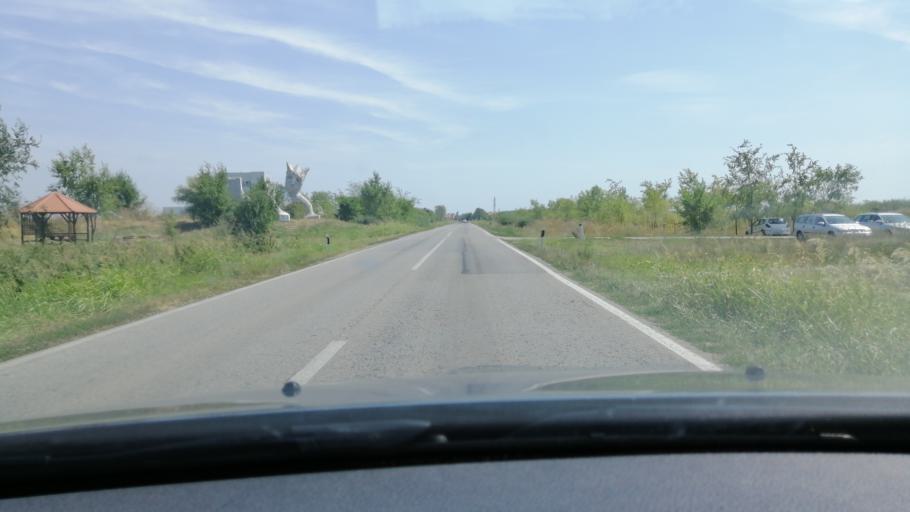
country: RS
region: Autonomna Pokrajina Vojvodina
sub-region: Srednjebanatski Okrug
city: Secanj
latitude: 45.3711
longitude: 20.7522
